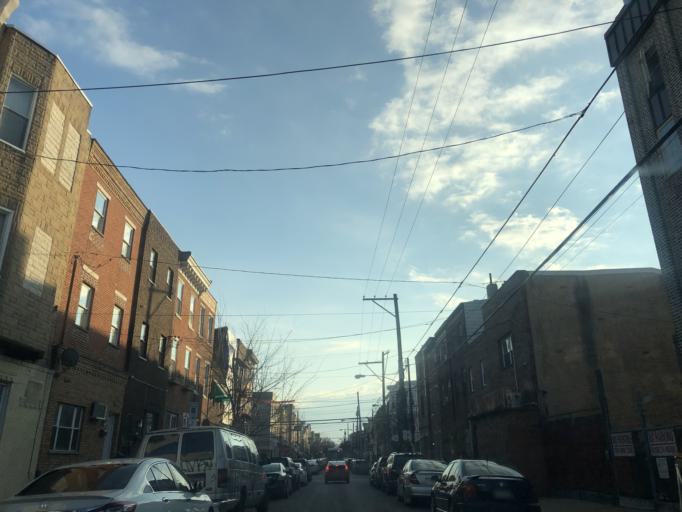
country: US
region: Pennsylvania
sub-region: Philadelphia County
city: Philadelphia
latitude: 39.9335
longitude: -75.1575
